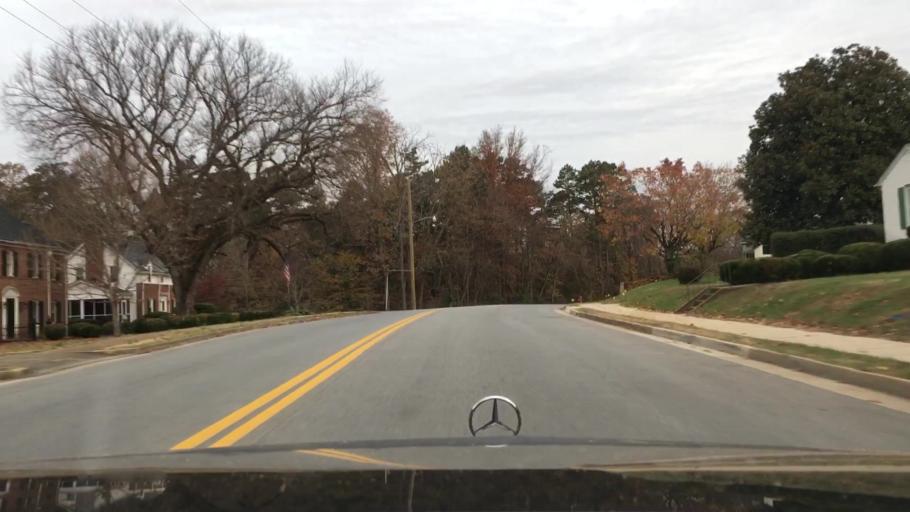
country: US
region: Virginia
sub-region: Campbell County
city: Altavista
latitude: 37.1161
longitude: -79.3008
